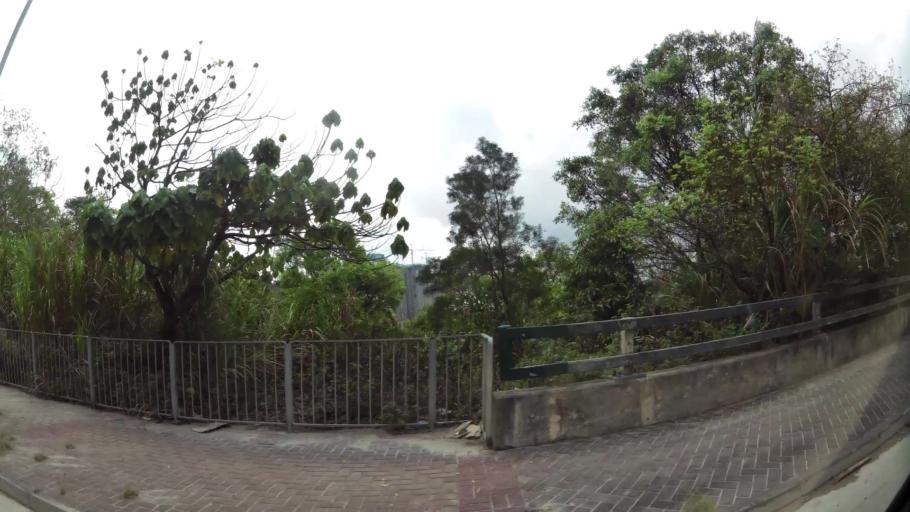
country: HK
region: Wong Tai Sin
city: Wong Tai Sin
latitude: 22.3340
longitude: 114.2264
